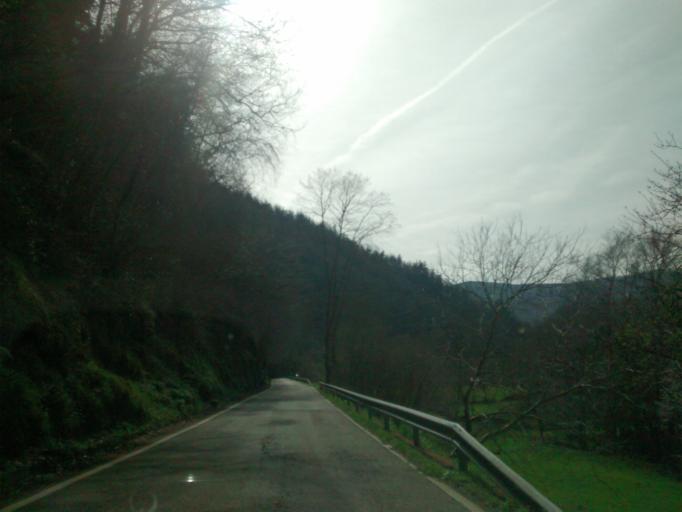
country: ES
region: Cantabria
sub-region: Provincia de Cantabria
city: San Pedro del Romeral
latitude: 43.1707
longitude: -3.8739
